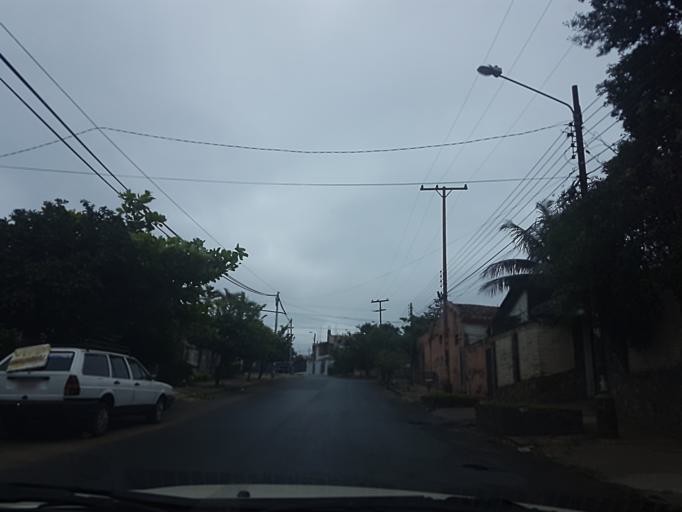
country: PY
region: Central
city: Lambare
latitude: -25.3214
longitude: -57.5982
